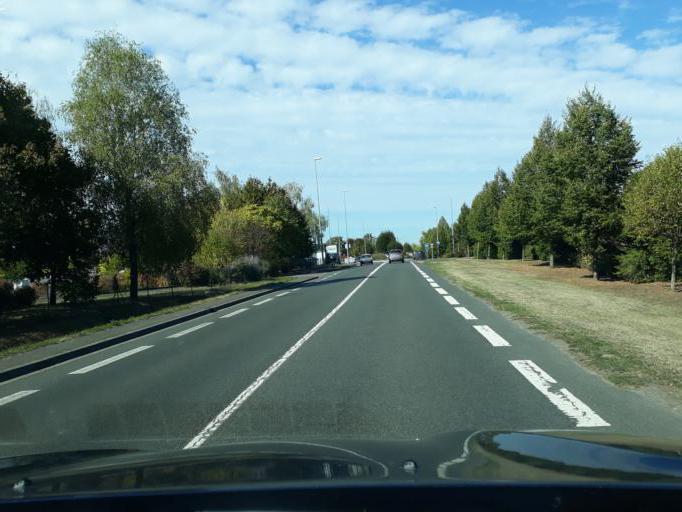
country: FR
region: Centre
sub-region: Departement d'Indre-et-Loire
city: Saint-Avertin
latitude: 47.3409
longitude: 0.7385
